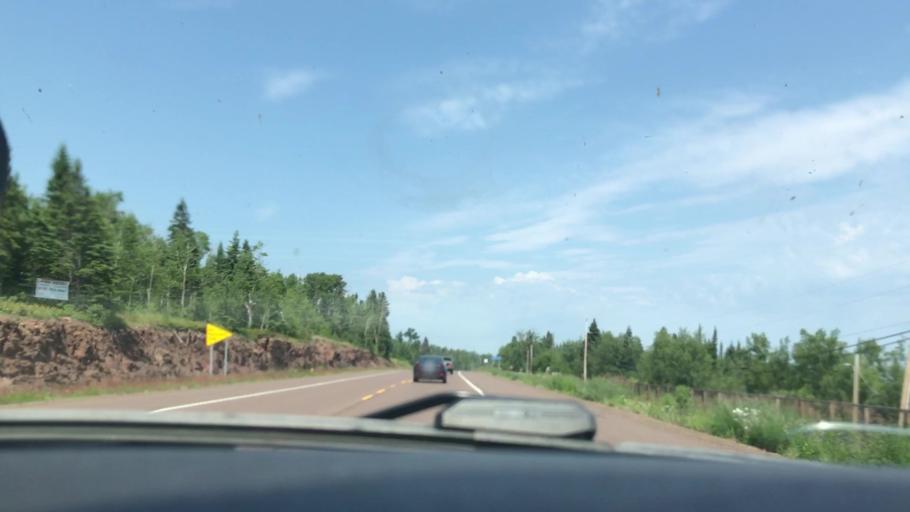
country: US
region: Minnesota
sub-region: Cook County
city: Grand Marais
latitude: 47.6021
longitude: -90.7847
